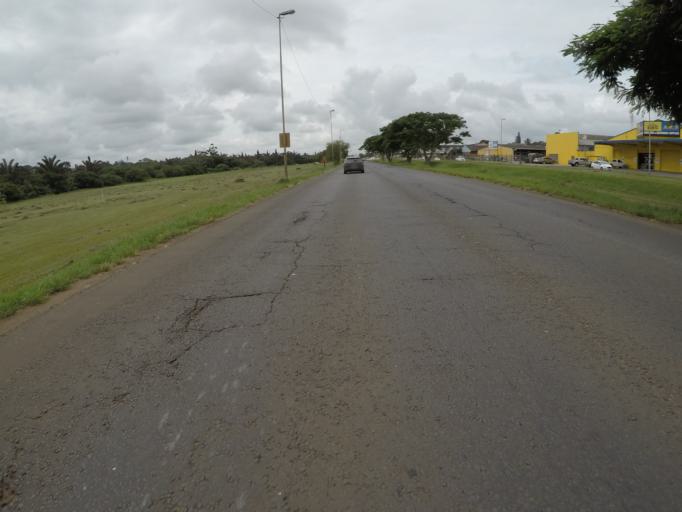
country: ZA
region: KwaZulu-Natal
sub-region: uThungulu District Municipality
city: Empangeni
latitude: -28.7704
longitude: 31.9029
